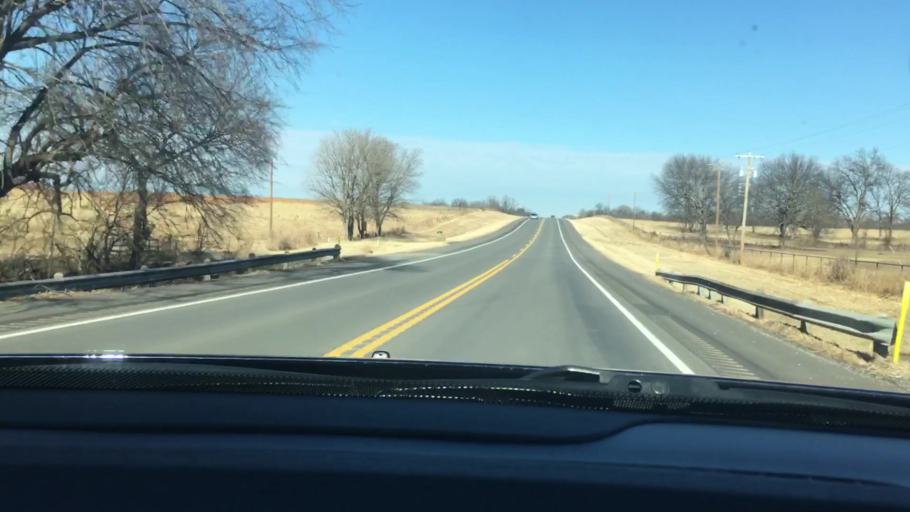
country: US
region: Oklahoma
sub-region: Murray County
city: Davis
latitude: 34.5517
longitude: -97.1328
